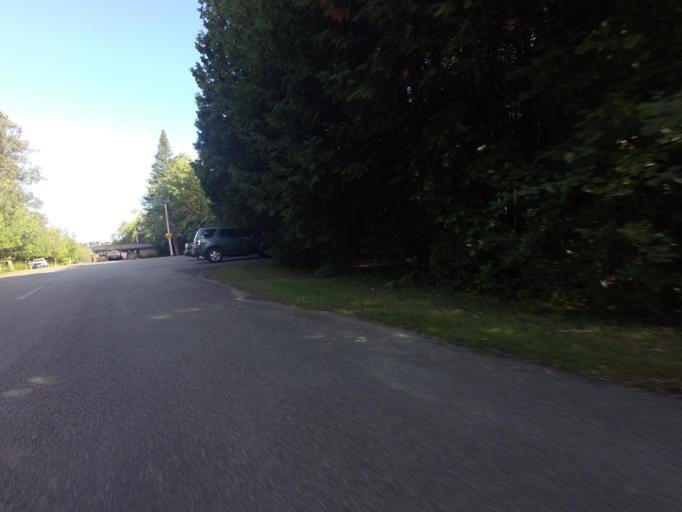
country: CA
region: Ontario
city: Waterloo
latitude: 43.6714
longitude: -80.4439
